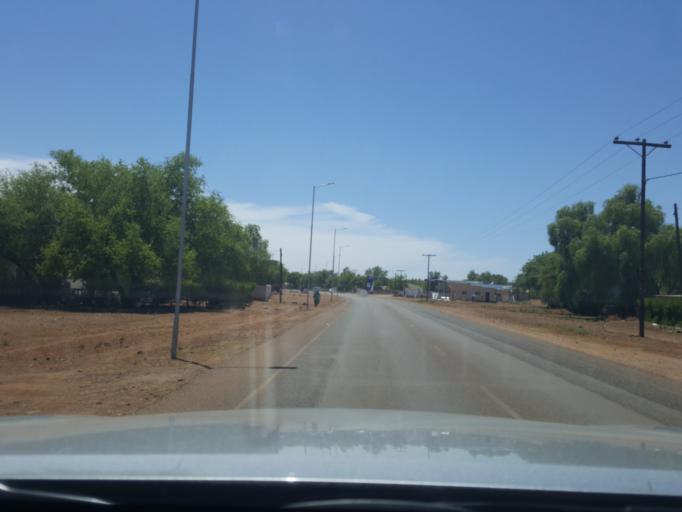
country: BW
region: South East
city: Ramotswa
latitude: -24.8675
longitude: 25.8692
